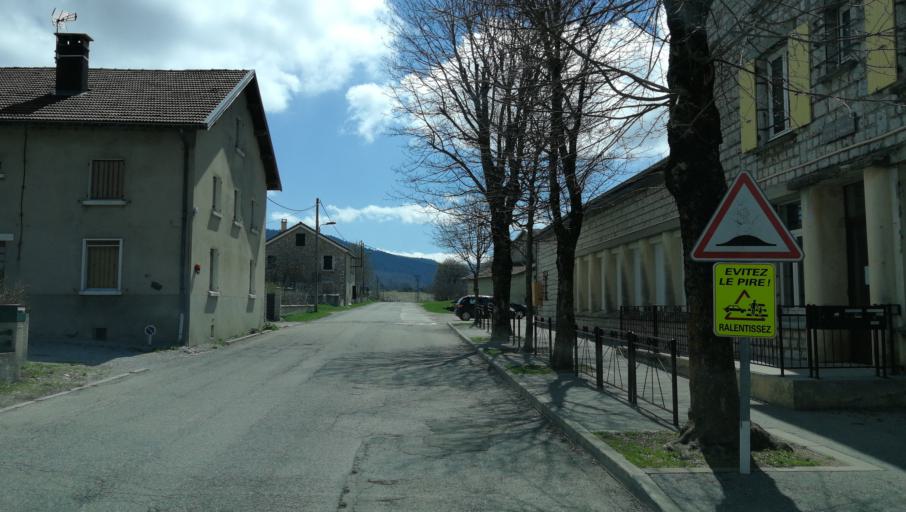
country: FR
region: Rhone-Alpes
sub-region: Departement de la Drome
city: Saint-Laurent-en-Royans
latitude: 44.8951
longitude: 5.3713
